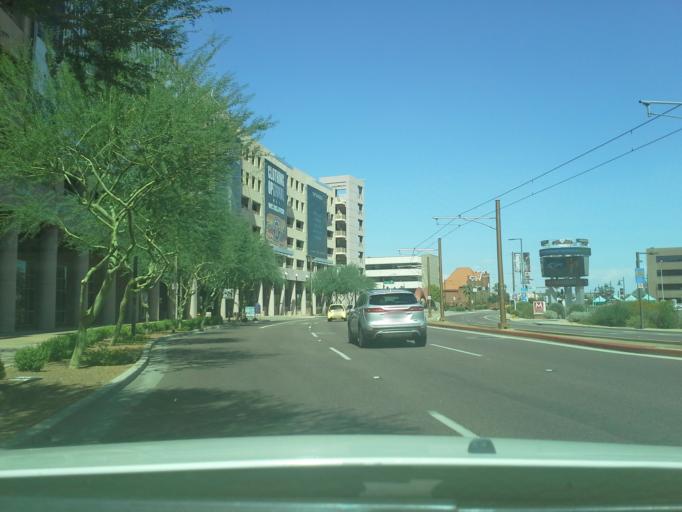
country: US
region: Arizona
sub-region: Maricopa County
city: Phoenix
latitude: 33.4468
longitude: -112.0669
